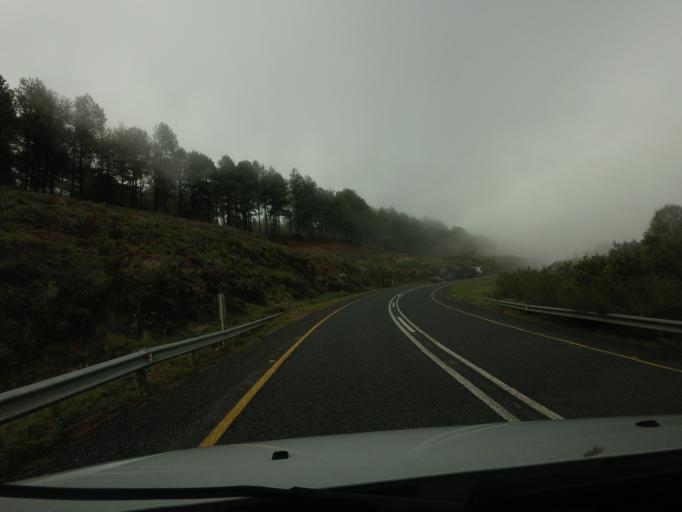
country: ZA
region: Mpumalanga
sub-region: Ehlanzeni District
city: Lydenburg
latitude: -25.1627
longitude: 30.6303
